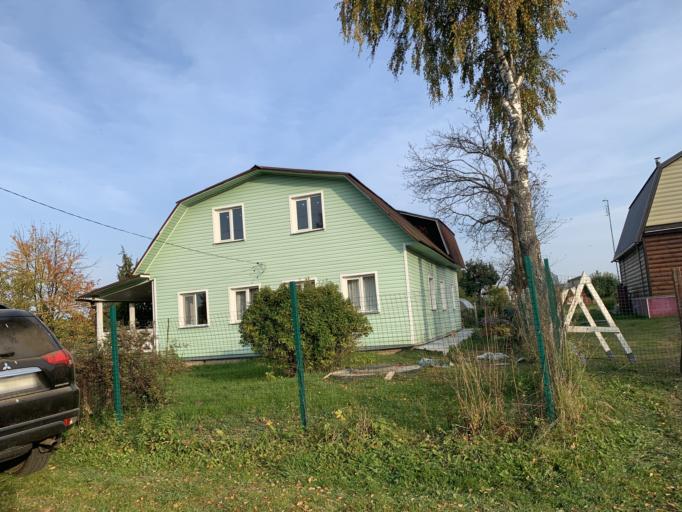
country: RU
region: Jaroslavl
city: Porech'ye-Rybnoye
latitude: 56.9809
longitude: 39.3841
